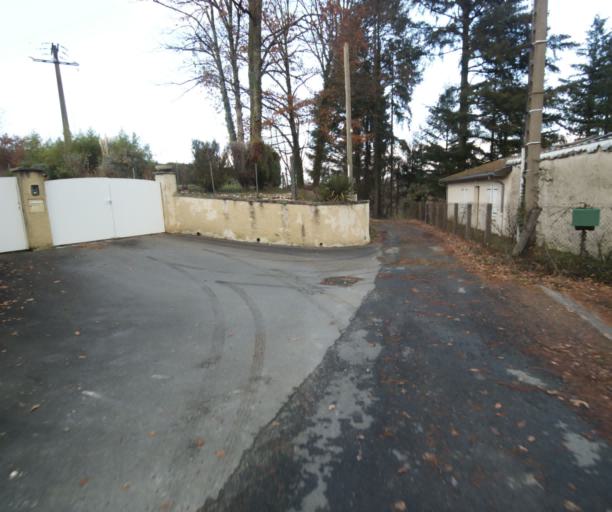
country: FR
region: Limousin
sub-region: Departement de la Correze
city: Laguenne
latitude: 45.2301
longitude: 1.7802
